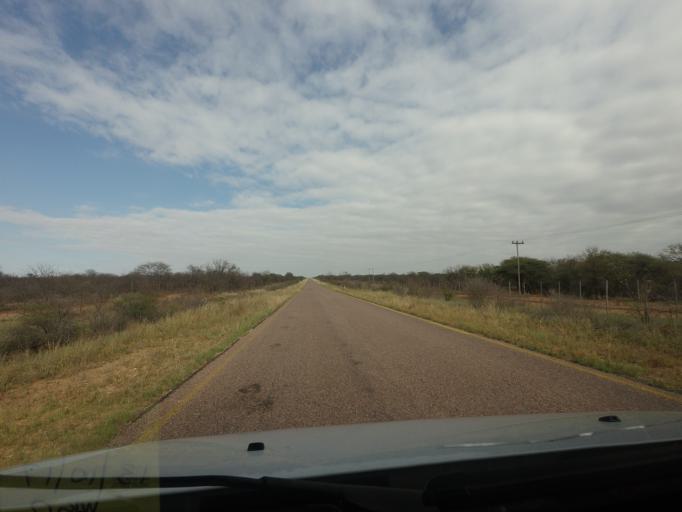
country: ZA
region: Limpopo
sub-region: Vhembe District Municipality
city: Messina
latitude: -22.6534
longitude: 29.9568
